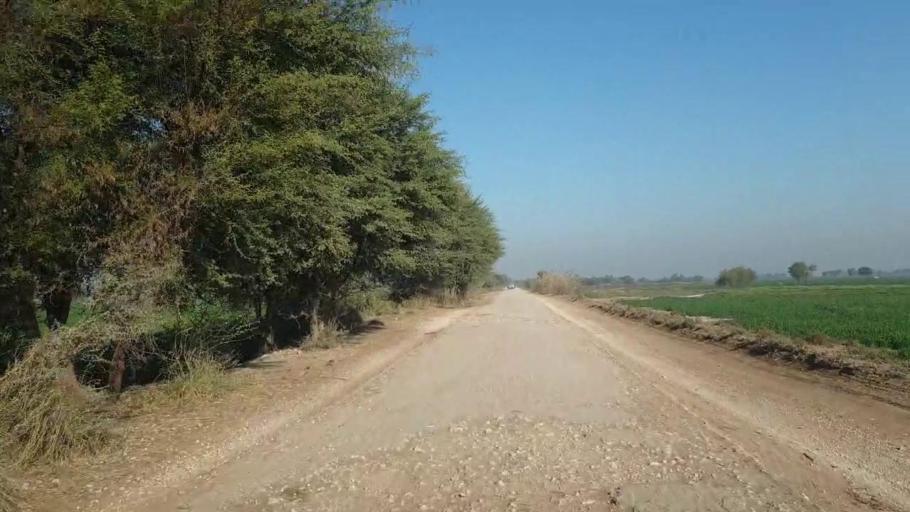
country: PK
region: Sindh
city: Shahdadpur
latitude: 25.9266
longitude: 68.5061
